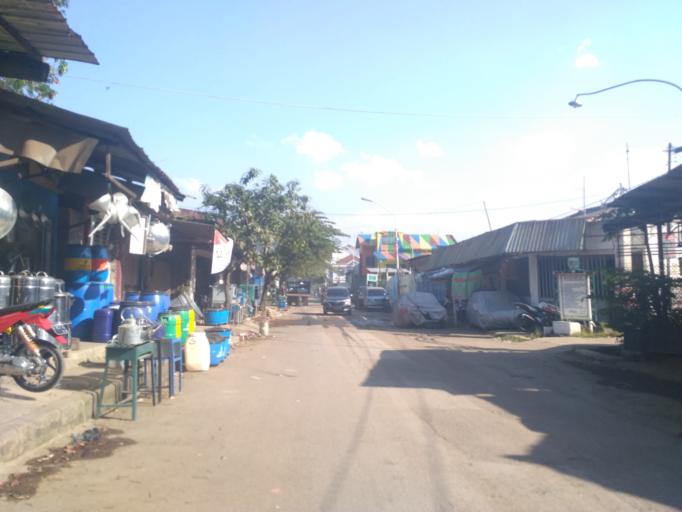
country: ID
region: Central Java
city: Semarang
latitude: -6.9770
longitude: 110.4415
